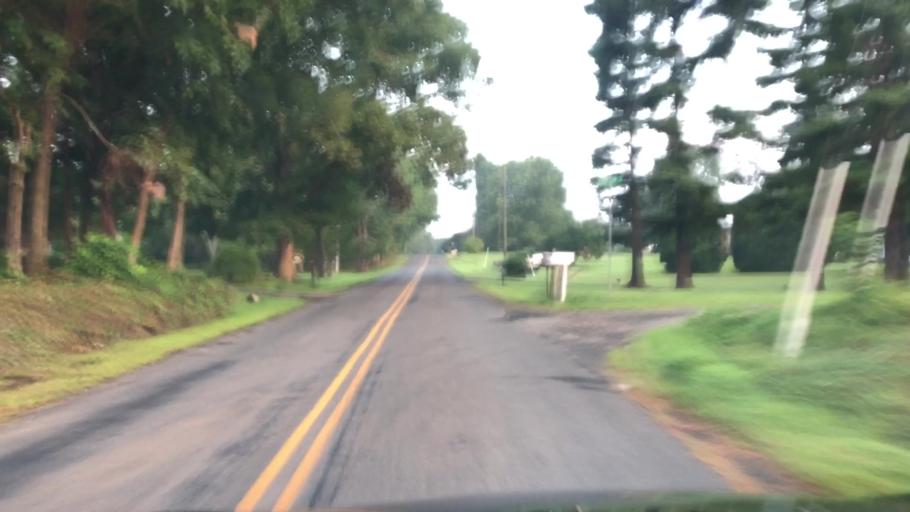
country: US
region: Virginia
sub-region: Fauquier County
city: New Baltimore
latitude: 38.7306
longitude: -77.6651
